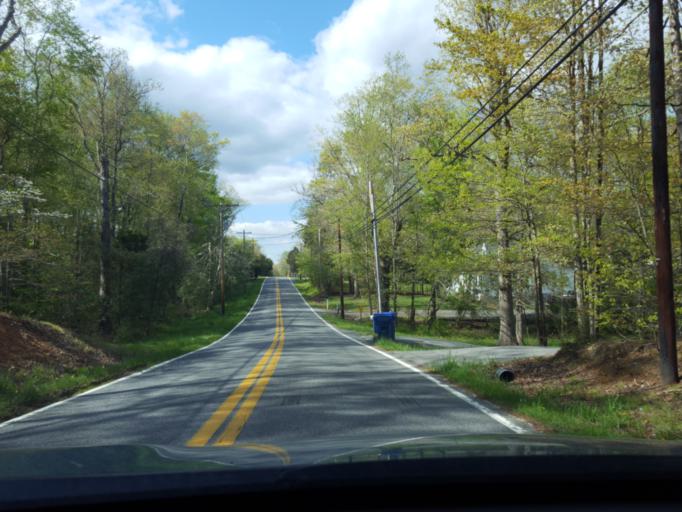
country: US
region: Maryland
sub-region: Charles County
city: La Plata
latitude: 38.4920
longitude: -76.9856
